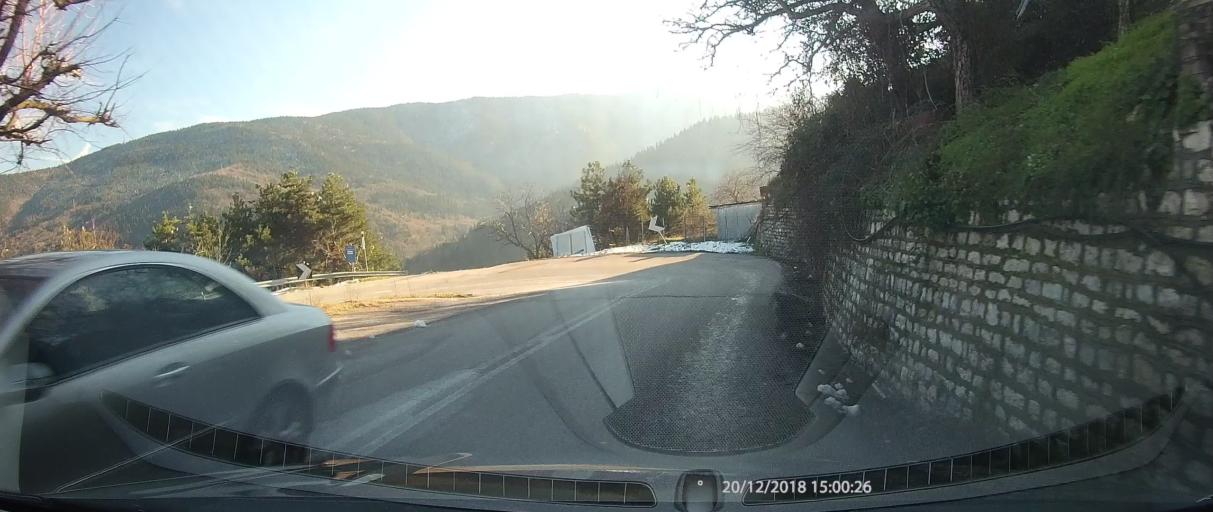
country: GR
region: Central Greece
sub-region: Nomos Evrytanias
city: Karpenisi
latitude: 38.9083
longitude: 21.9169
